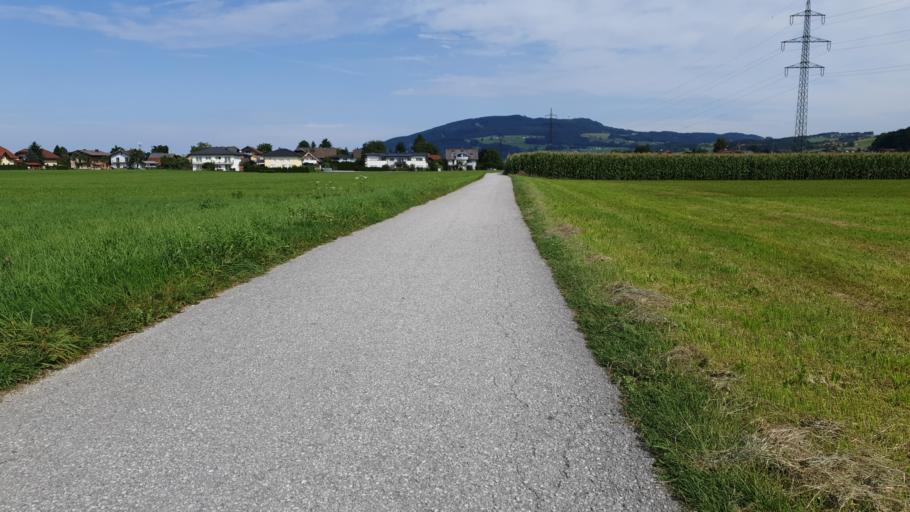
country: AT
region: Salzburg
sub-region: Politischer Bezirk Salzburg-Umgebung
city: Anthering
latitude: 47.8571
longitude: 13.0134
